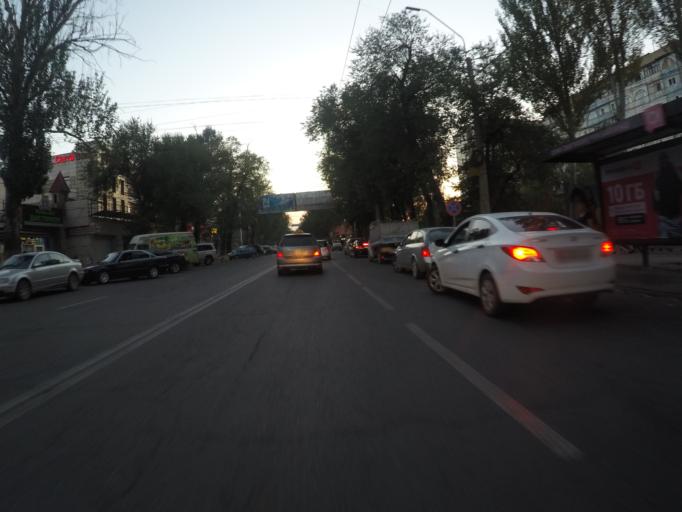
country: KG
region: Chuy
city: Bishkek
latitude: 42.8570
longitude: 74.6090
